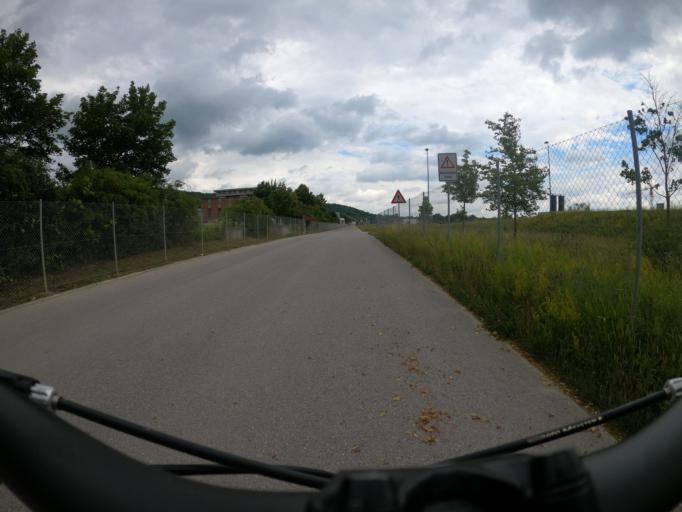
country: DE
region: Bavaria
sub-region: Swabia
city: Neu-Ulm
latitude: 48.4227
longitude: 10.0307
